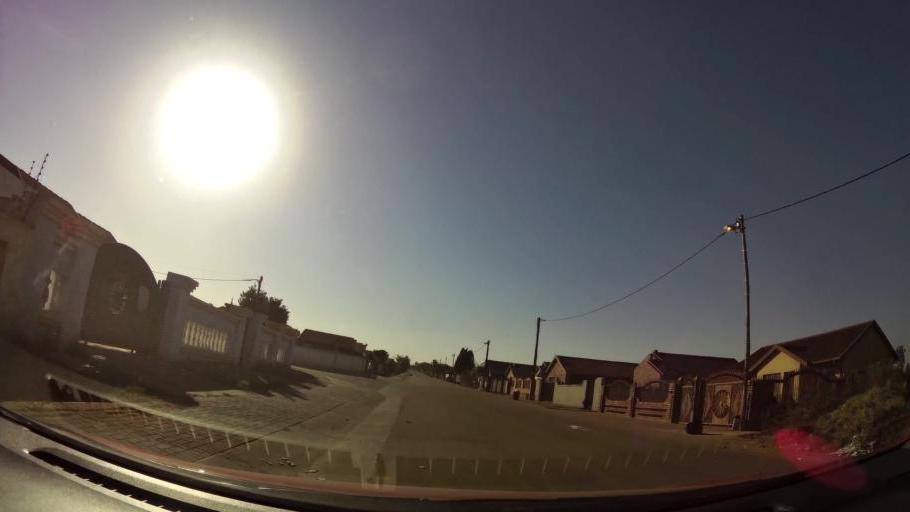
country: ZA
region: Gauteng
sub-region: City of Tshwane Metropolitan Municipality
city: Mabopane
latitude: -25.5868
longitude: 28.1104
